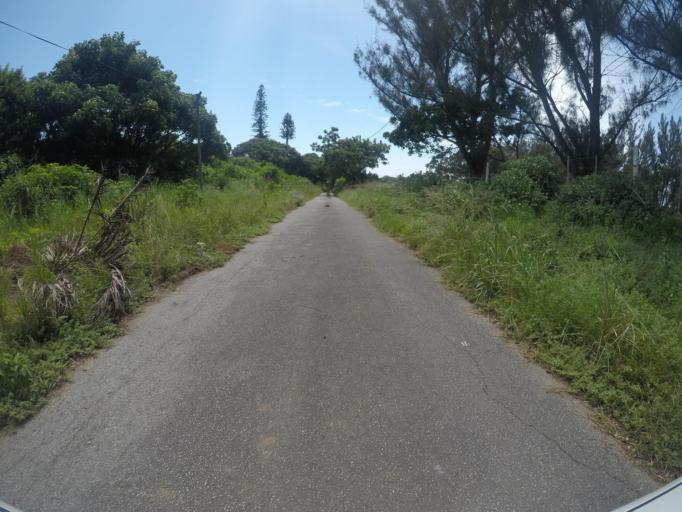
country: ZA
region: Eastern Cape
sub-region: Buffalo City Metropolitan Municipality
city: East London
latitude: -32.9527
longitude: 28.0012
